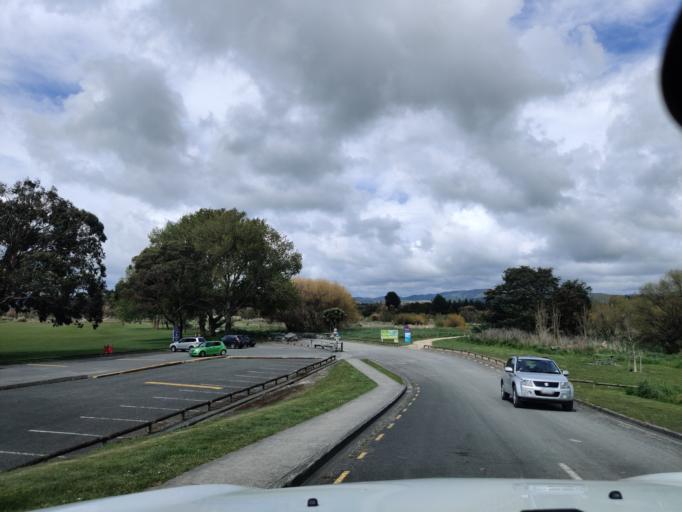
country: NZ
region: Manawatu-Wanganui
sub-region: Palmerston North City
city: Palmerston North
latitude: -40.3825
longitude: 175.5871
